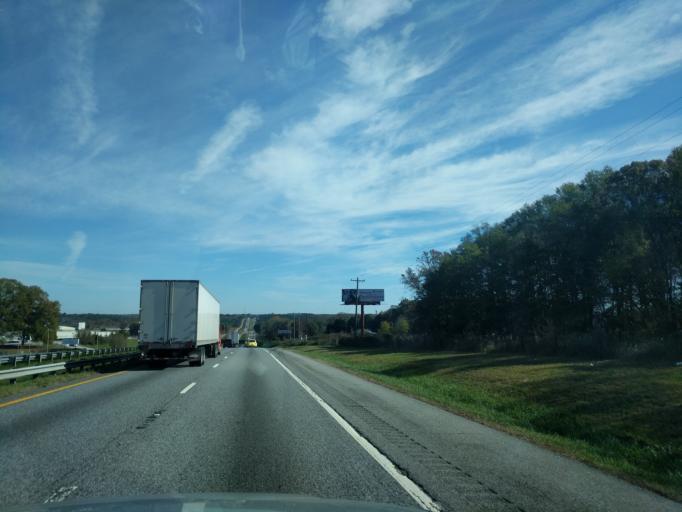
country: US
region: South Carolina
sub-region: Spartanburg County
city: Mayo
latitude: 35.0294
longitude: -81.8641
